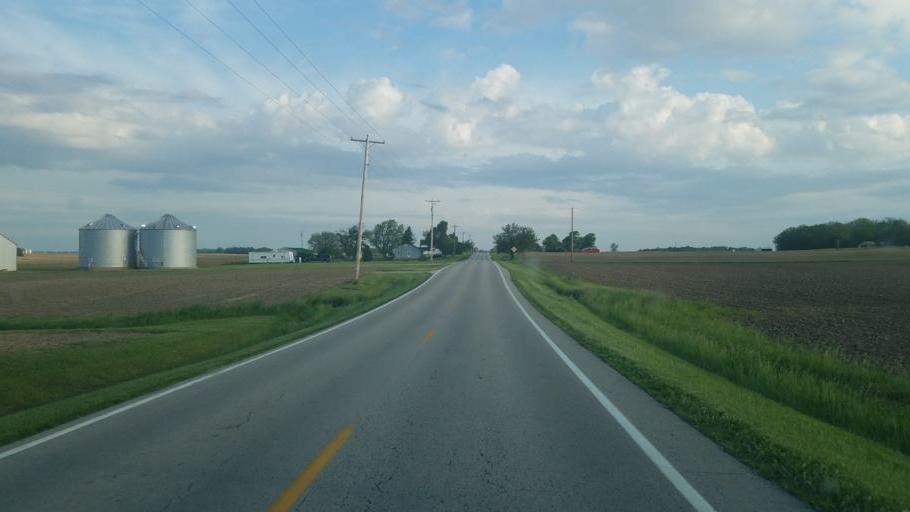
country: US
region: Ohio
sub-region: Clinton County
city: Sabina
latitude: 39.4234
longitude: -83.6220
